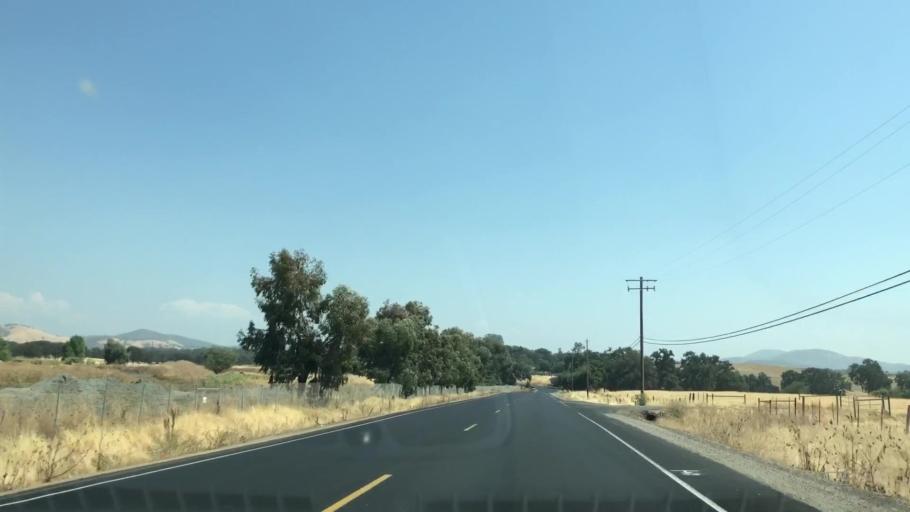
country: US
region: California
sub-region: Tuolumne County
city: Jamestown
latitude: 37.8792
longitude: -120.4534
